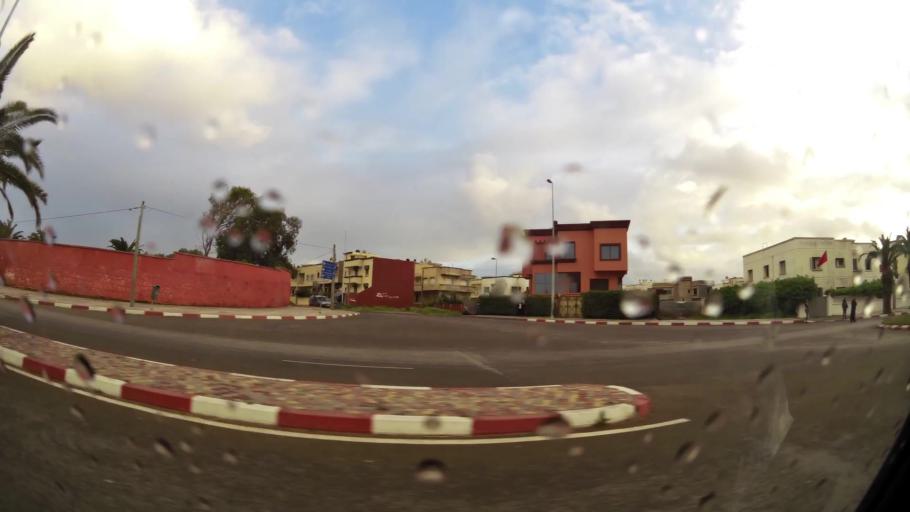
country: MA
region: Doukkala-Abda
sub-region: El-Jadida
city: El Jadida
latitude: 33.2416
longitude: -8.5030
